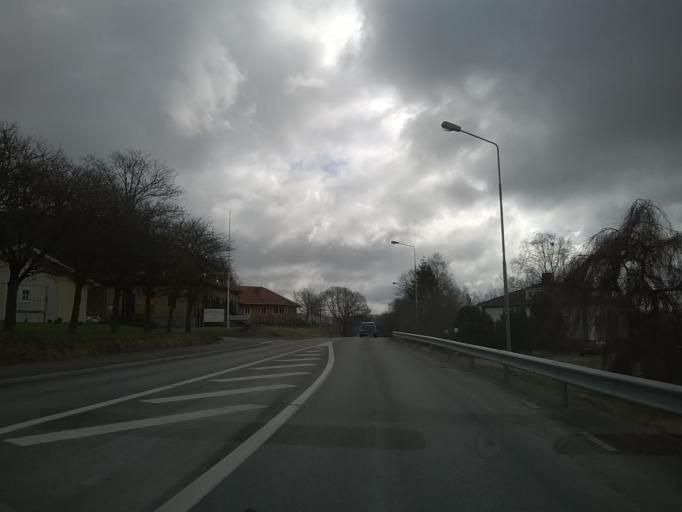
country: SE
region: Halland
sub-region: Varbergs Kommun
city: Tvaaker
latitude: 57.1439
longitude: 12.4609
